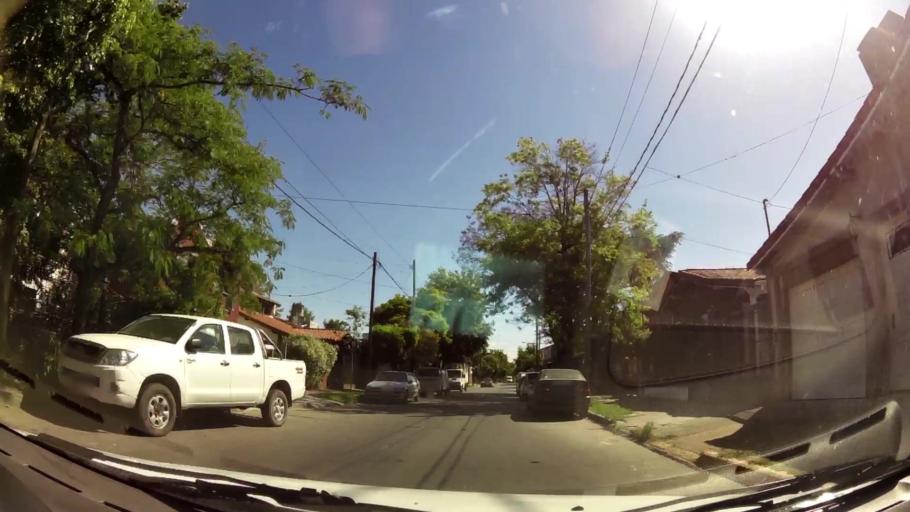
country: AR
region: Buenos Aires
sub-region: Partido de San Isidro
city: San Isidro
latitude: -34.4533
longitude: -58.5294
